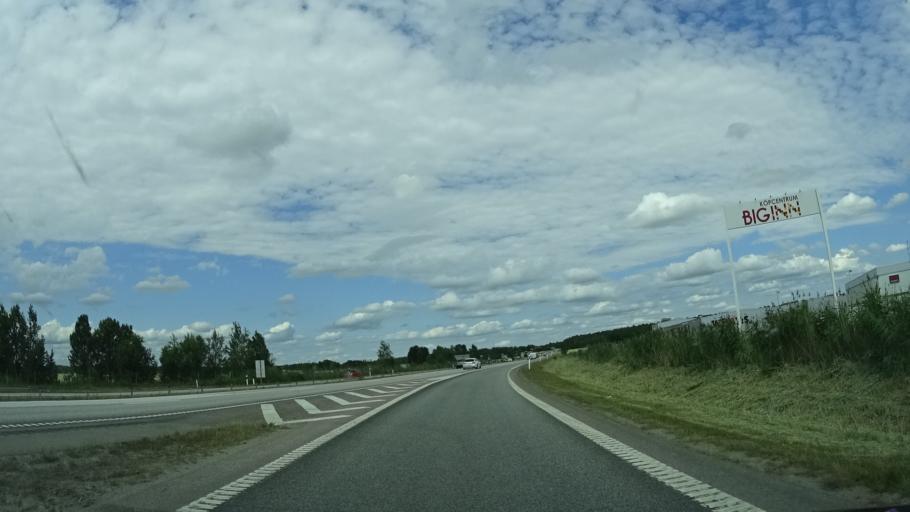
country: SE
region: Vaestmanland
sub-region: Kopings Kommun
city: Koping
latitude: 59.5224
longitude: 15.9717
